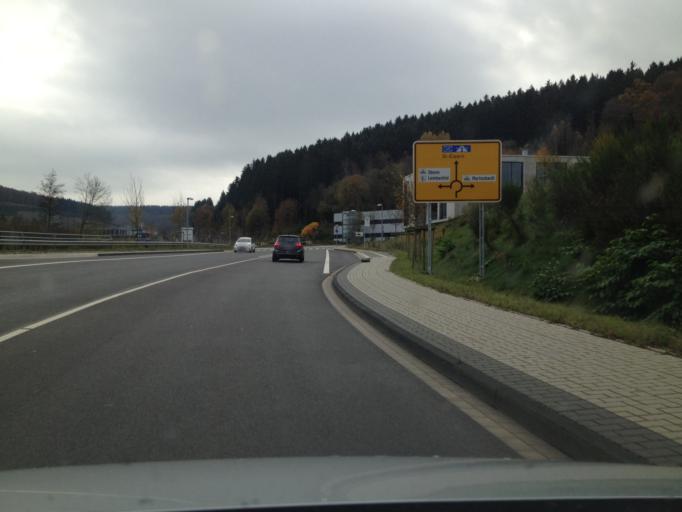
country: DE
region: North Rhine-Westphalia
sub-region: Regierungsbezirk Arnsberg
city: Siegen
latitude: 50.8519
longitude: 8.0323
